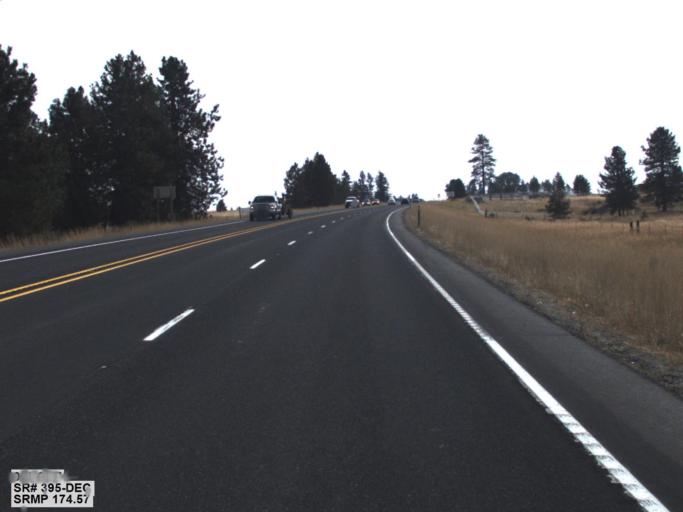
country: US
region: Washington
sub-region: Spokane County
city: Deer Park
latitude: 47.8816
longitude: -117.4224
